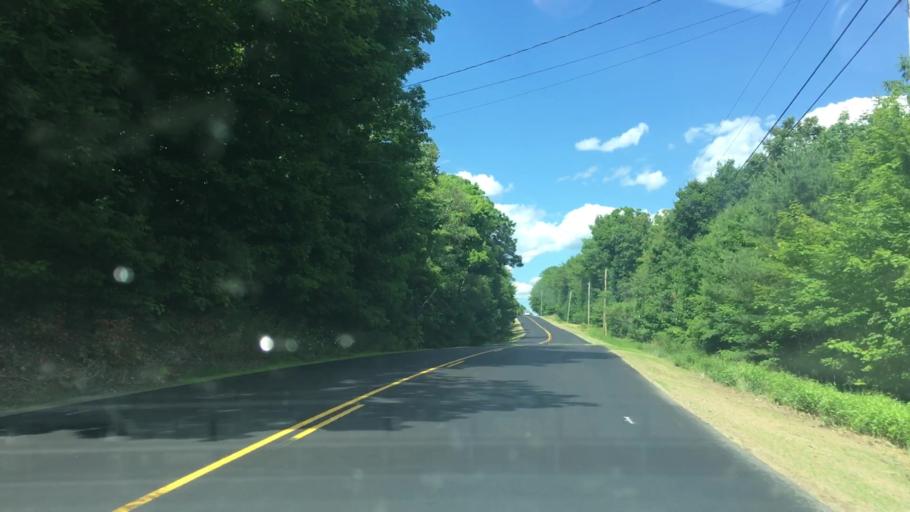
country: US
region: Maine
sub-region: Franklin County
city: Jay
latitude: 44.5486
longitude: -70.1883
